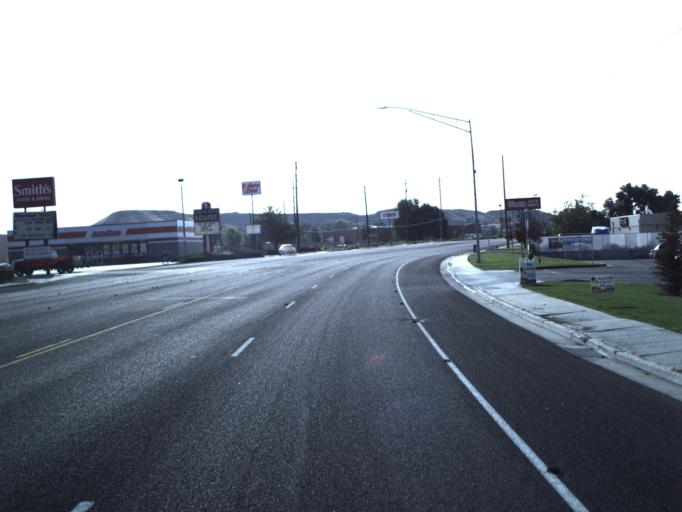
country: US
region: Utah
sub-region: Carbon County
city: Price
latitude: 39.5991
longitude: -110.7950
